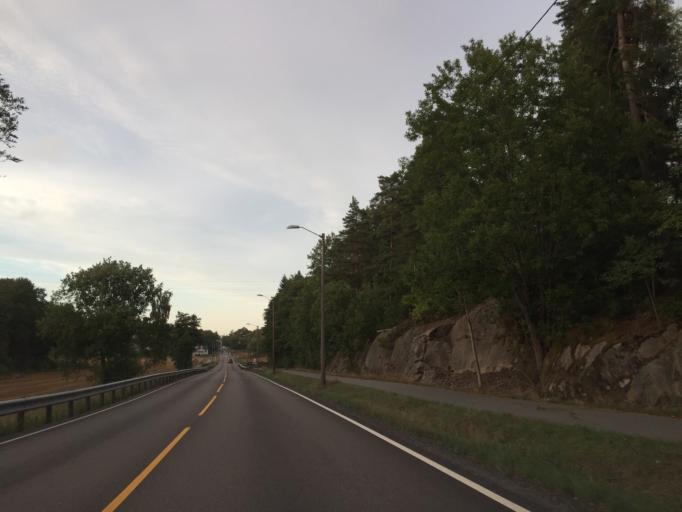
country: NO
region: Ostfold
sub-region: Fredrikstad
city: Fredrikstad
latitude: 59.1884
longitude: 10.9335
